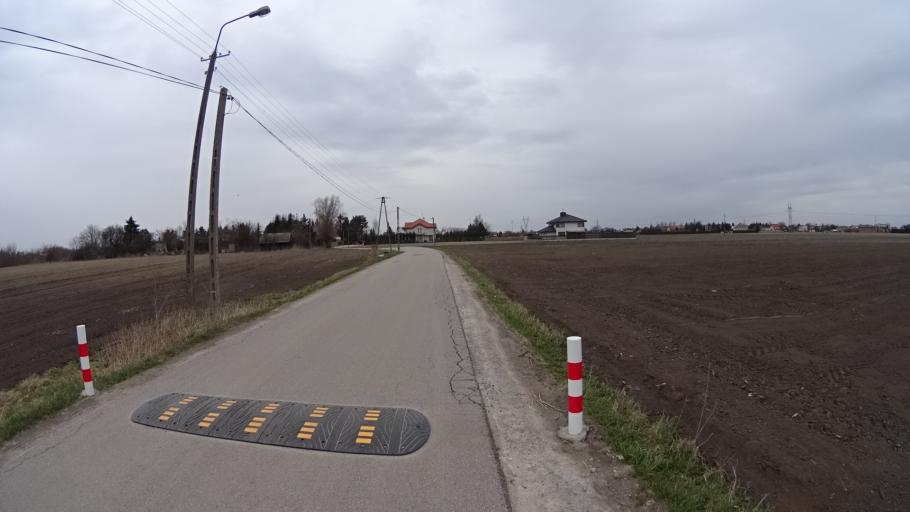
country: PL
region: Masovian Voivodeship
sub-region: Powiat warszawski zachodni
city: Stare Babice
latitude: 52.2429
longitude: 20.8251
